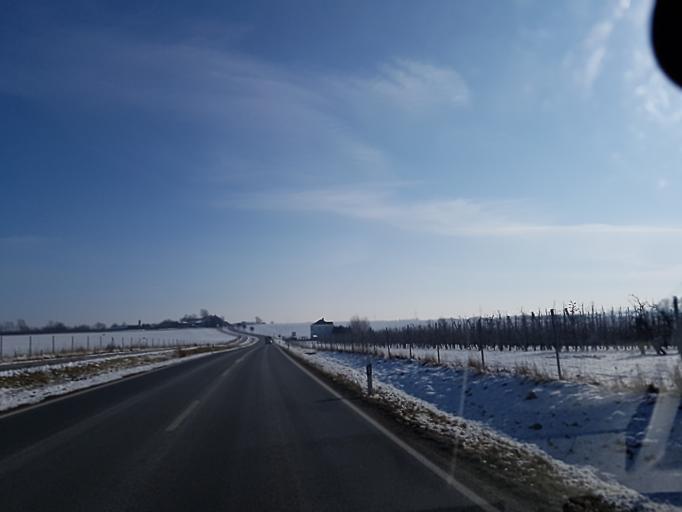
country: DE
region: Saxony
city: Leisnig
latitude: 51.1448
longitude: 12.9394
